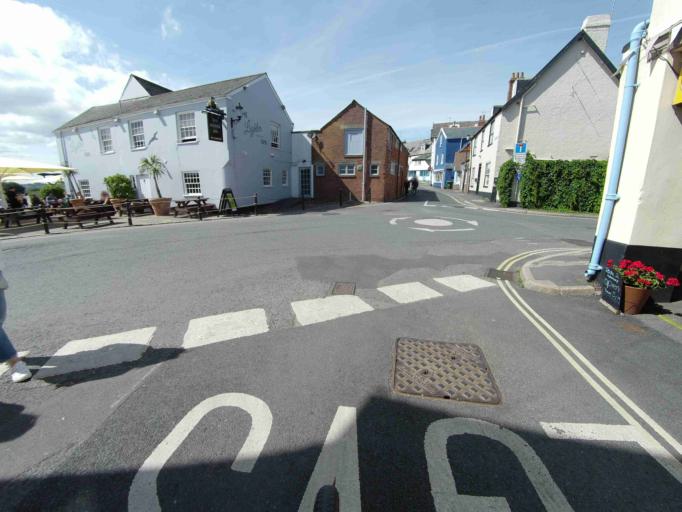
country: GB
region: England
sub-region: Devon
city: Topsham
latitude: 50.6813
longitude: -3.4645
